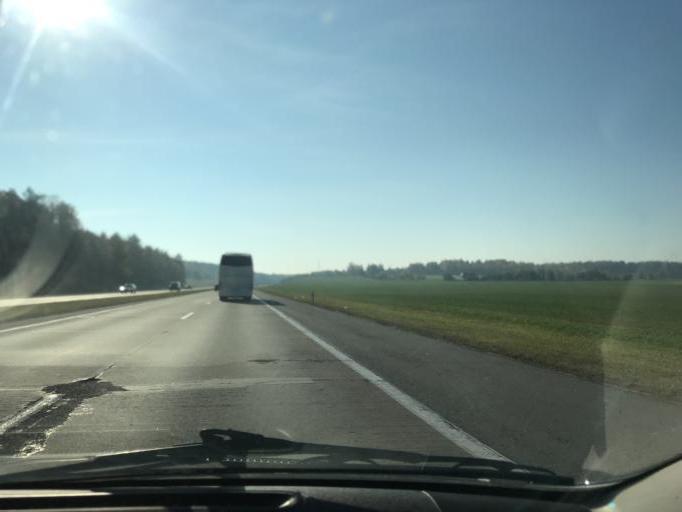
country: BY
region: Minsk
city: Samakhvalavichy
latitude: 53.5532
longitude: 27.4753
